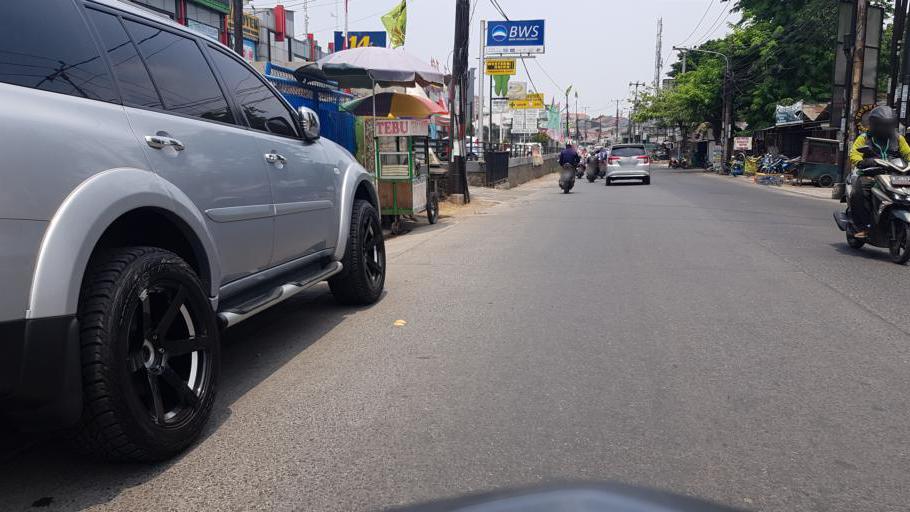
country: ID
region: West Java
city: Bekasi
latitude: -6.2856
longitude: 106.9187
